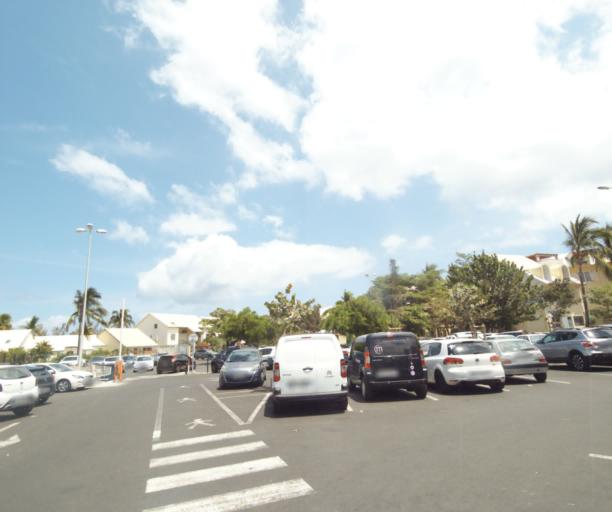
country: RE
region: Reunion
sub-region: Reunion
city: Saint-Paul
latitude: -21.0741
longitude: 55.2227
